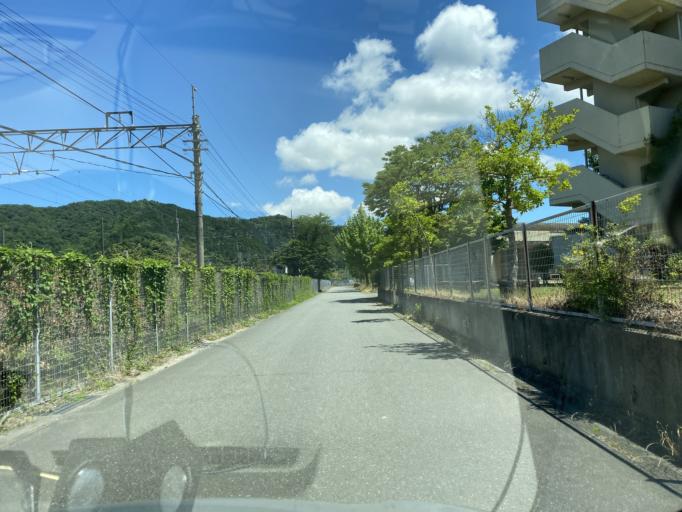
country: JP
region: Hyogo
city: Toyooka
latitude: 35.4950
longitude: 134.7995
